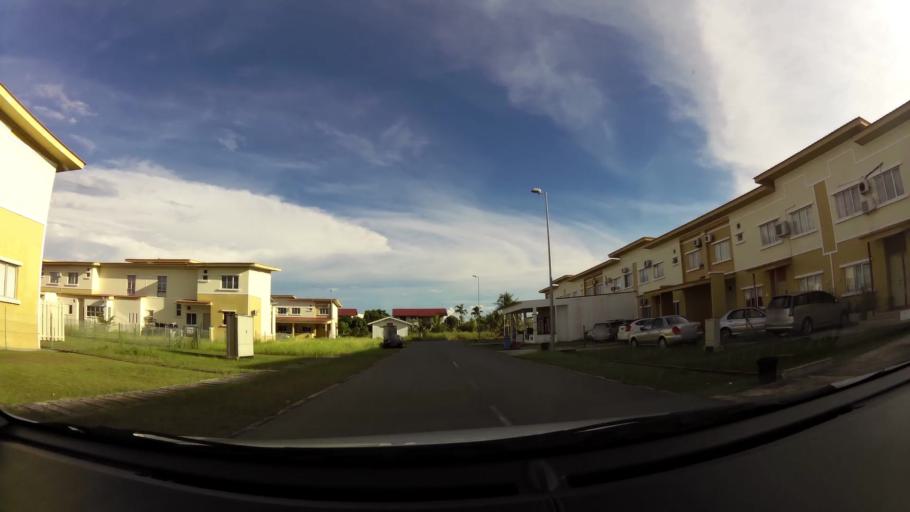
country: BN
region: Belait
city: Kuala Belait
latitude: 4.5793
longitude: 114.2207
